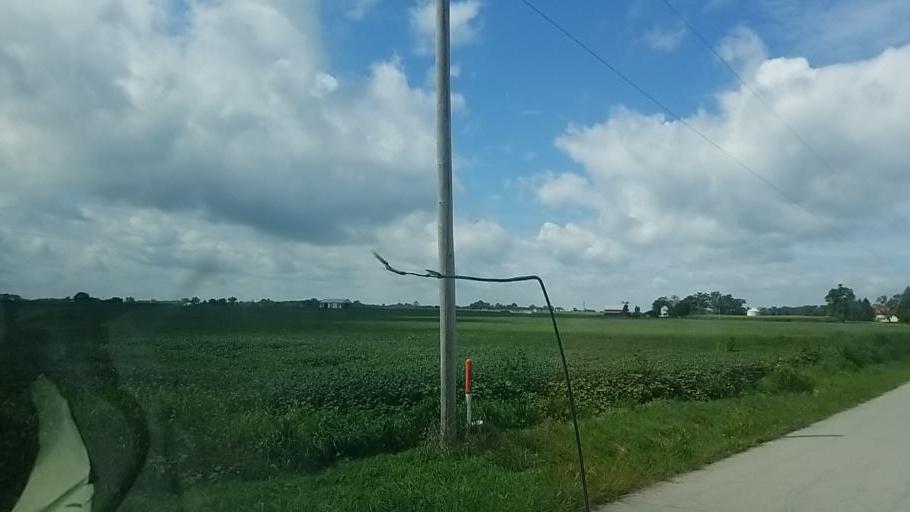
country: US
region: Ohio
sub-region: Fayette County
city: Jeffersonville
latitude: 39.6853
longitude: -83.4987
